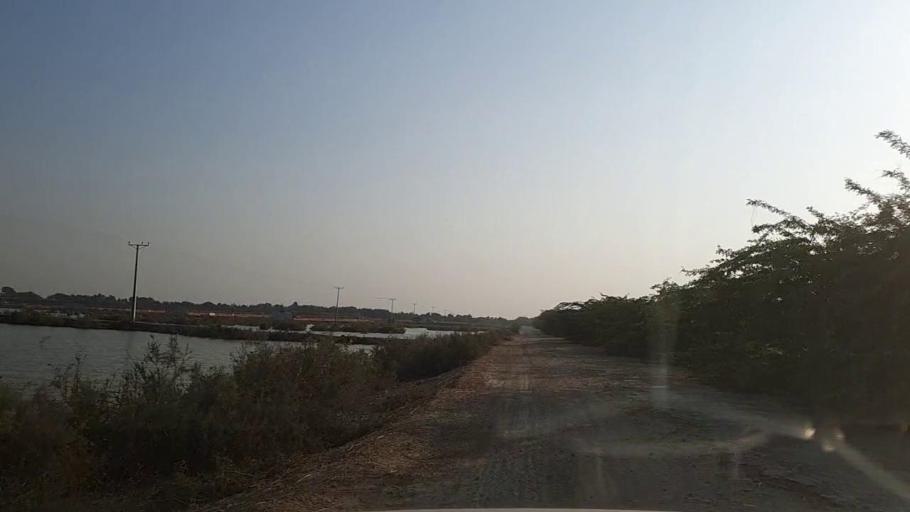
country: PK
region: Sindh
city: Mirpur Batoro
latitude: 24.7602
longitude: 68.2319
